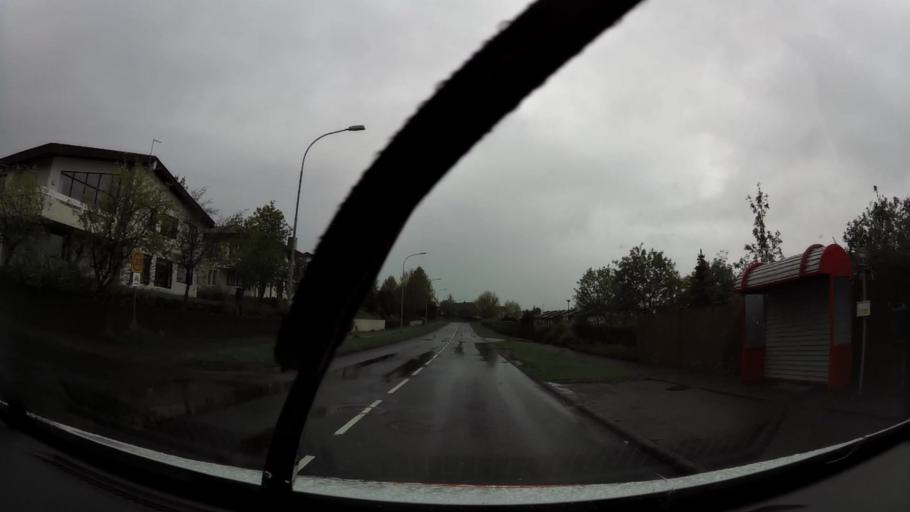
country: IS
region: Capital Region
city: Reykjavik
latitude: 64.0939
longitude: -21.8417
